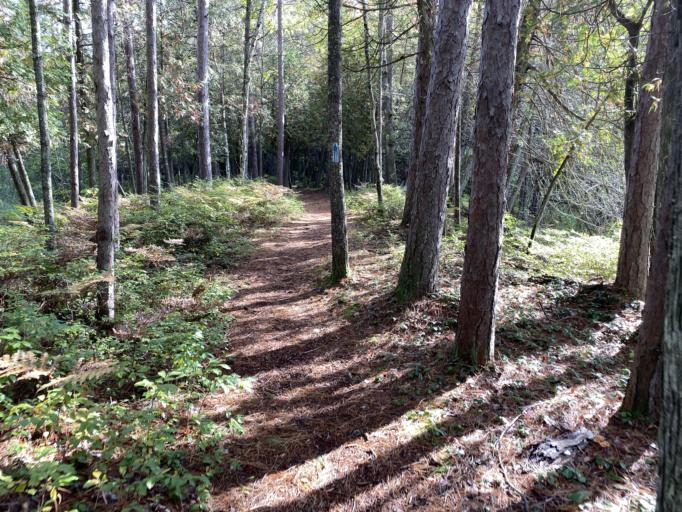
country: US
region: Michigan
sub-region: Mackinac County
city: Saint Ignace
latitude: 45.7453
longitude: -84.8811
